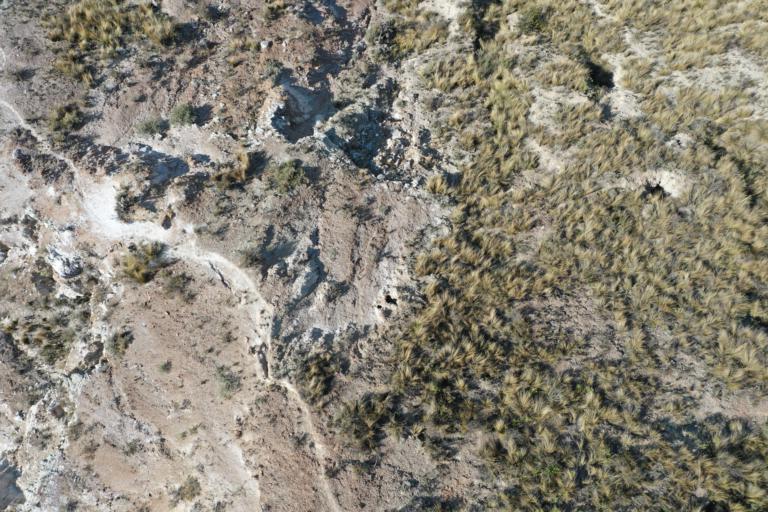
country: BO
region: La Paz
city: La Paz
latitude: -16.5598
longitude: -68.1225
